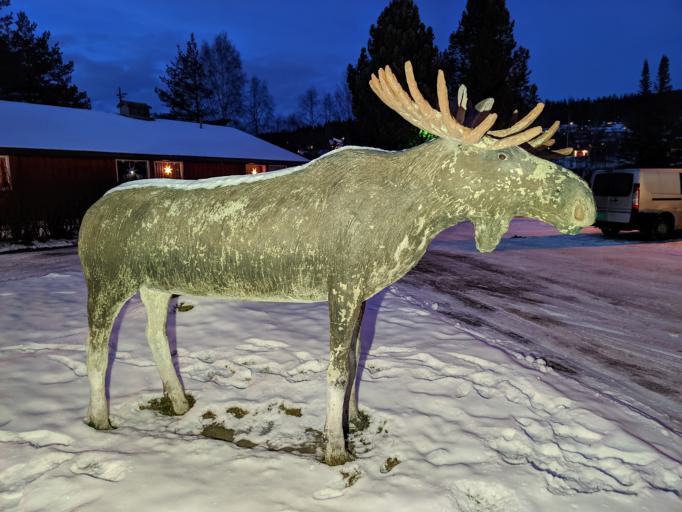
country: NO
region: Hedmark
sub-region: Stor-Elvdal
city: Koppang
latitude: 61.5711
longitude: 11.0506
